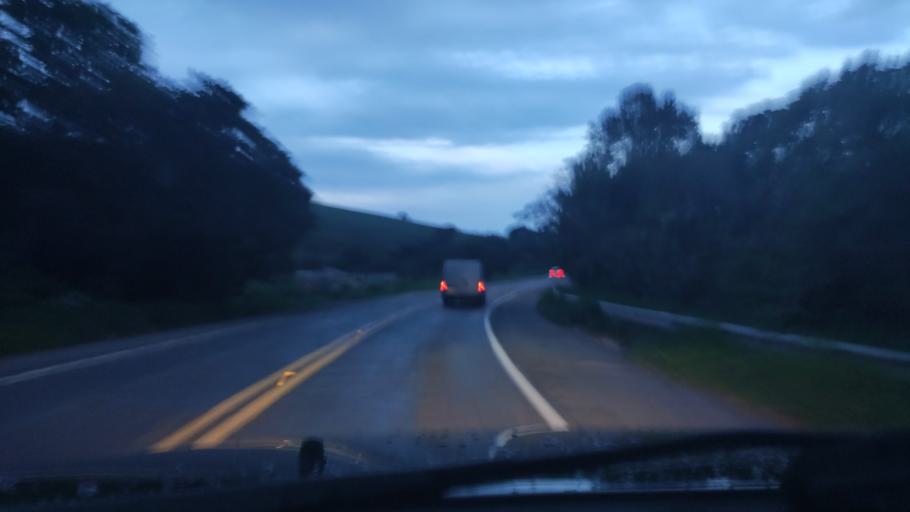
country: BR
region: Sao Paulo
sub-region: Socorro
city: Socorro
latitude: -22.6564
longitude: -46.5448
